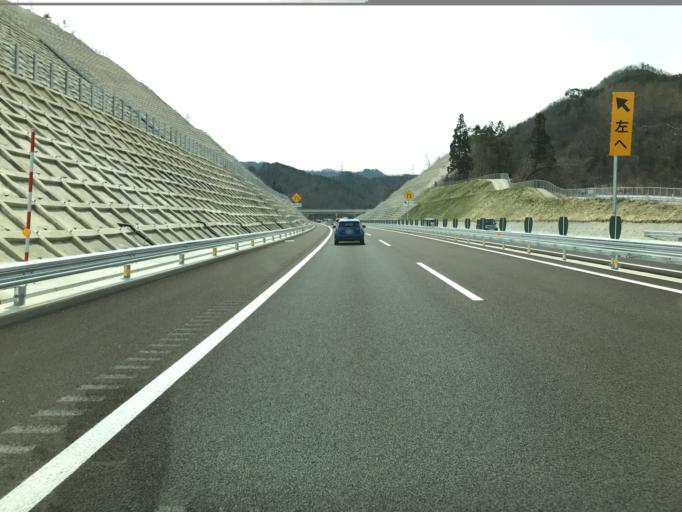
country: JP
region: Yamagata
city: Kaminoyama
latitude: 38.1218
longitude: 140.2508
